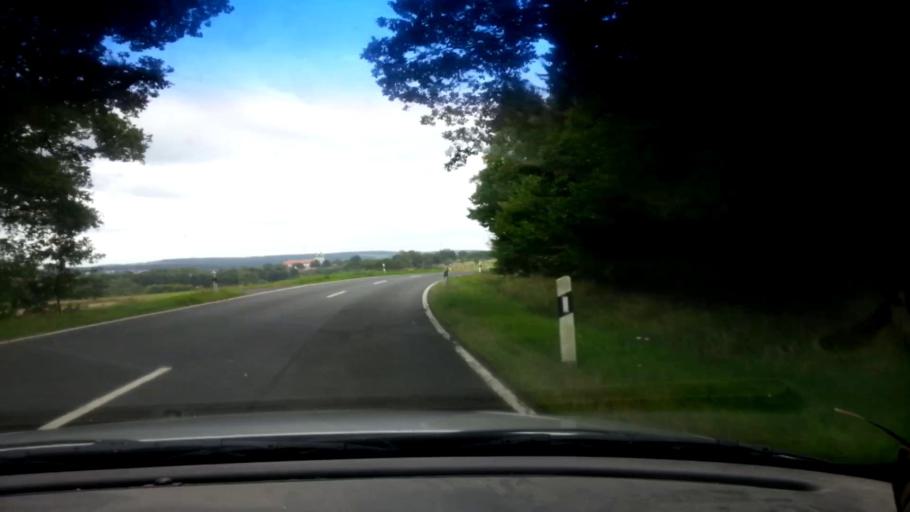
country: DE
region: Bavaria
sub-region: Upper Palatinate
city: Waldsassen
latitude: 50.0159
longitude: 12.3113
